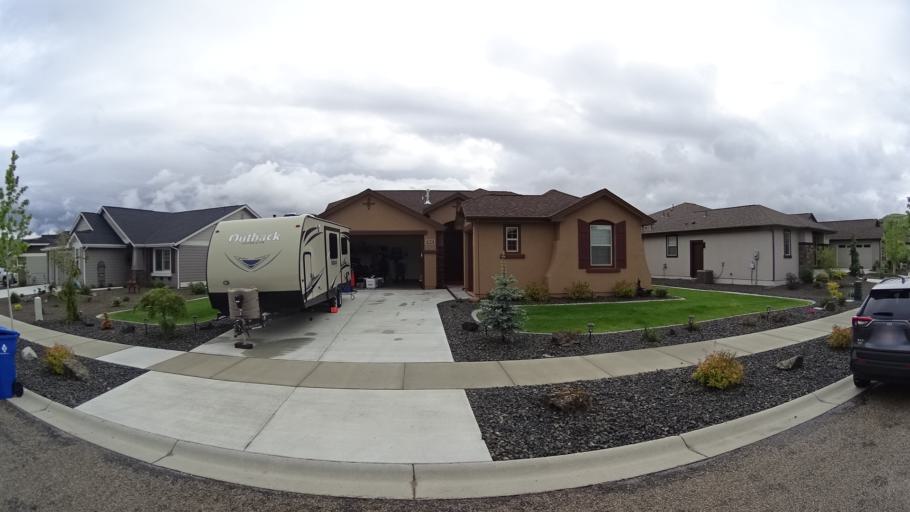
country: US
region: Idaho
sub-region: Ada County
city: Eagle
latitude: 43.7694
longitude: -116.2598
